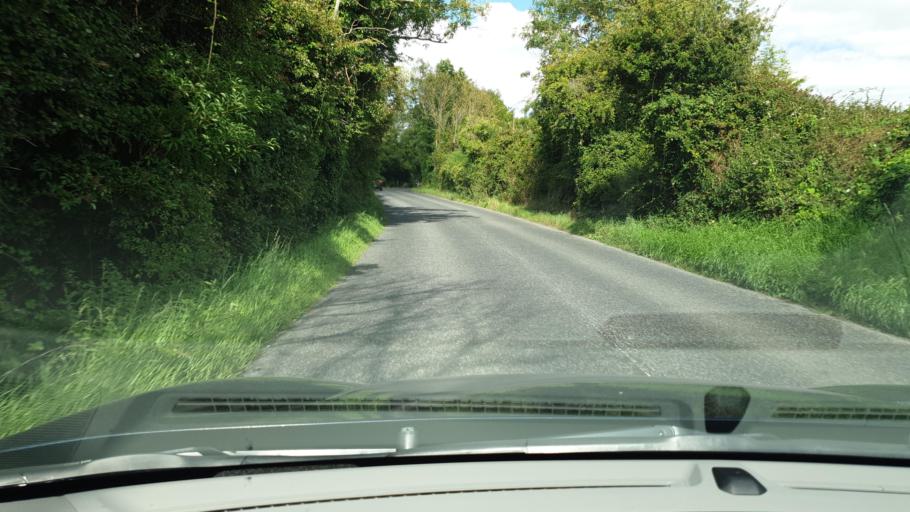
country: IE
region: Leinster
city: Lucan
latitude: 53.3732
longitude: -6.4428
